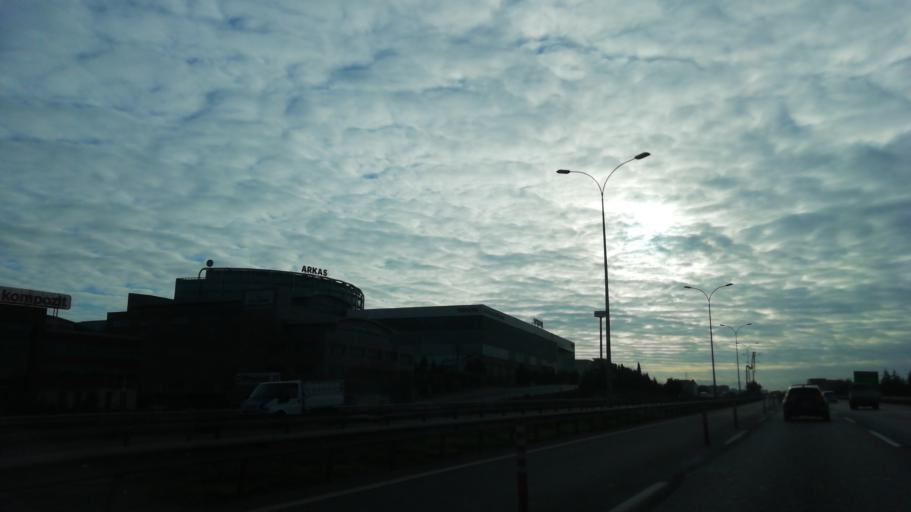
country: TR
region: Kocaeli
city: Balcik
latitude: 40.8851
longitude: 29.3763
